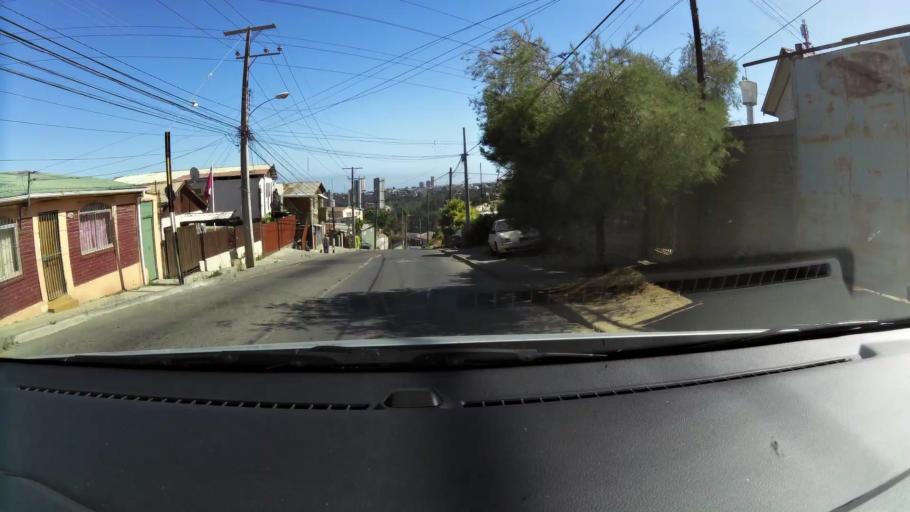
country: CL
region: Valparaiso
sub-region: Provincia de Valparaiso
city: Valparaiso
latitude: -33.0690
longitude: -71.5828
